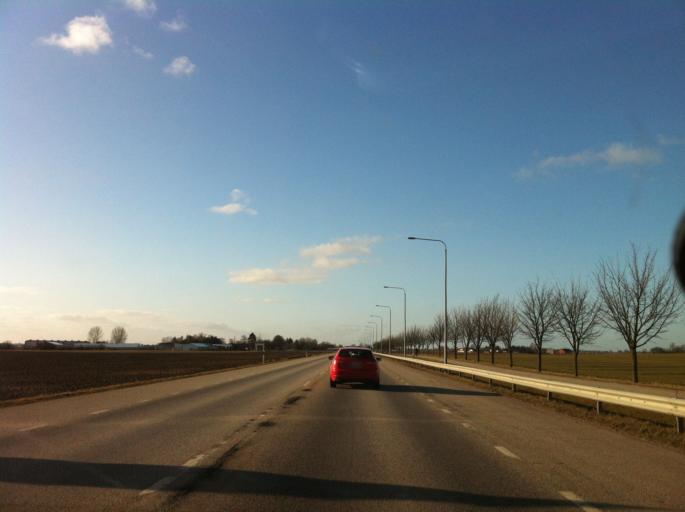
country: SE
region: Skane
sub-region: Svedala Kommun
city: Klagerup
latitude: 55.6245
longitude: 13.2518
